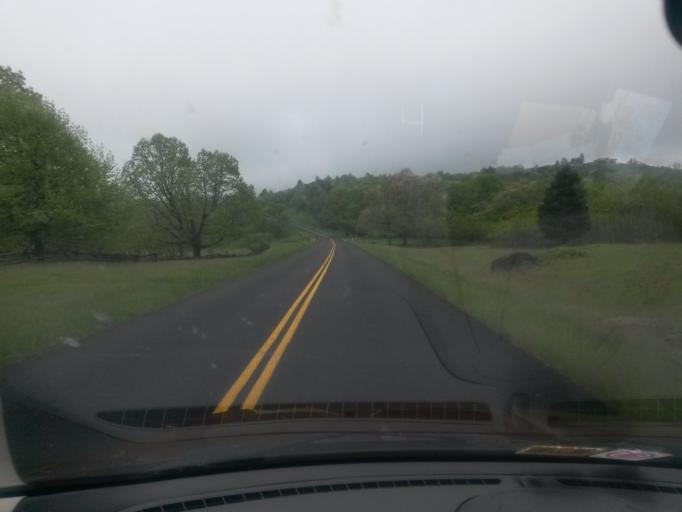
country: US
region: Virginia
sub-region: Floyd County
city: Floyd
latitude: 36.8038
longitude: -80.3666
